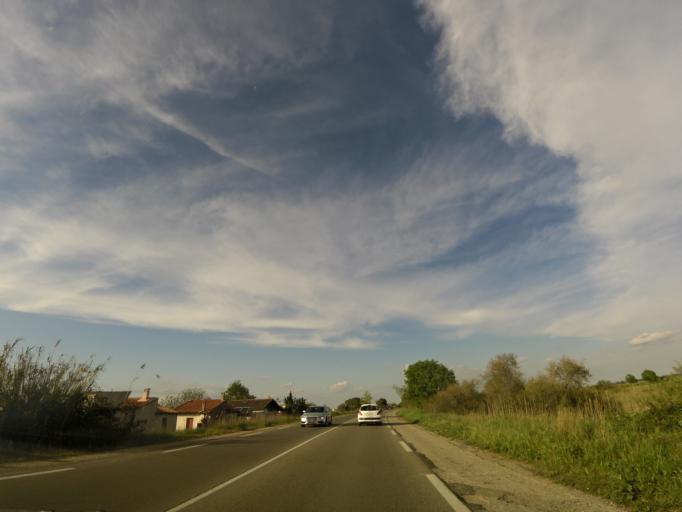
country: FR
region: Languedoc-Roussillon
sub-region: Departement de l'Herault
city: Candillargues
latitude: 43.6081
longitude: 4.1074
